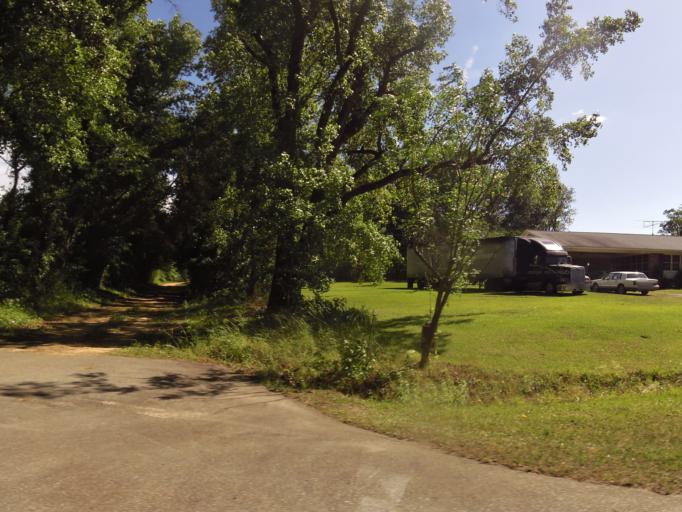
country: US
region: South Carolina
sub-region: Bamberg County
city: Denmark
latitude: 33.3455
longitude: -81.2016
